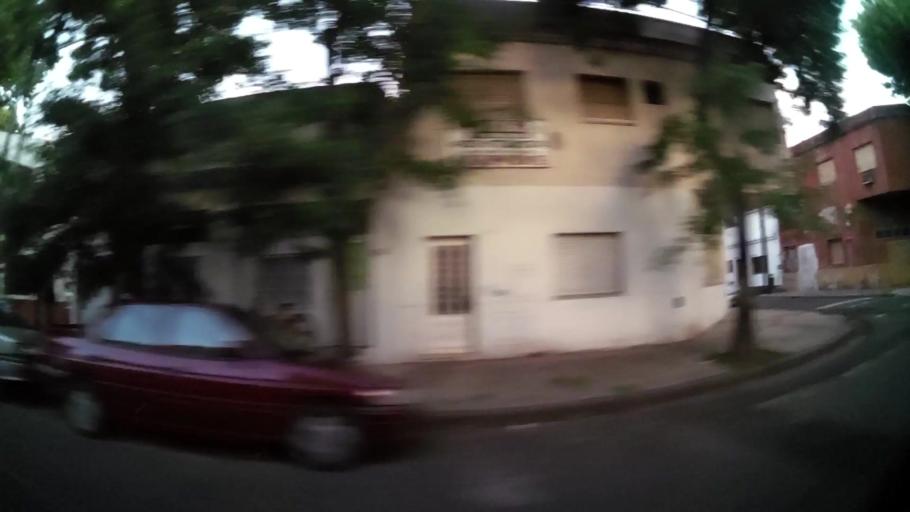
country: AR
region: Buenos Aires F.D.
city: Villa Santa Rita
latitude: -34.6392
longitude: -58.4357
